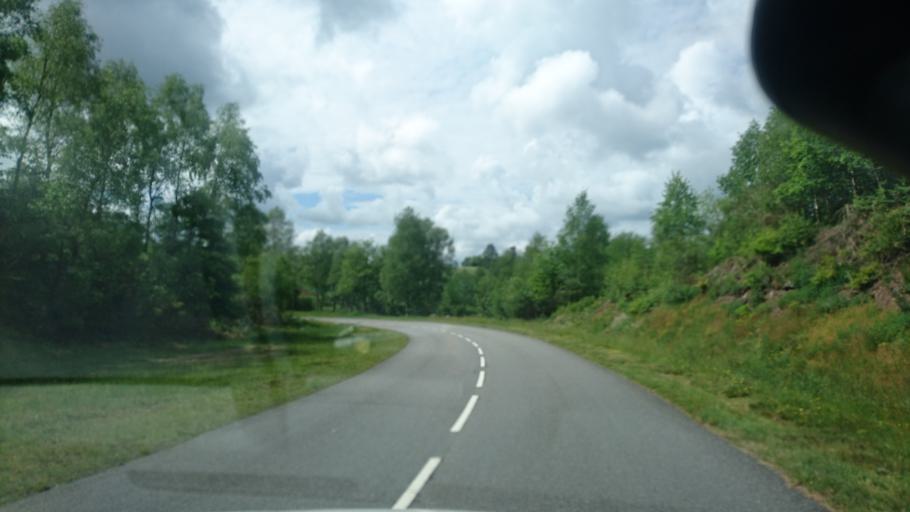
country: FR
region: Limousin
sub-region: Departement de la Haute-Vienne
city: Peyrat-le-Chateau
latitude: 45.7784
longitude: 1.8640
